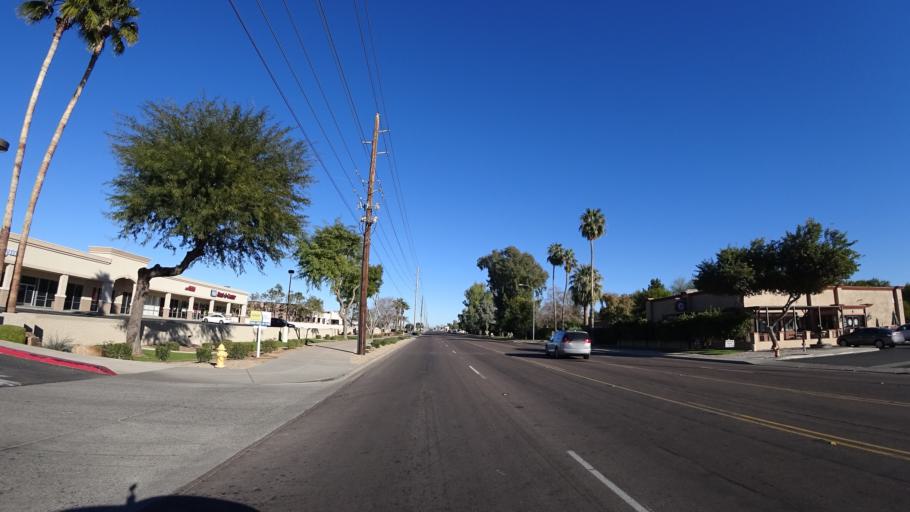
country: US
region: Arizona
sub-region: Maricopa County
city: Goodyear
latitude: 33.4499
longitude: -112.3567
